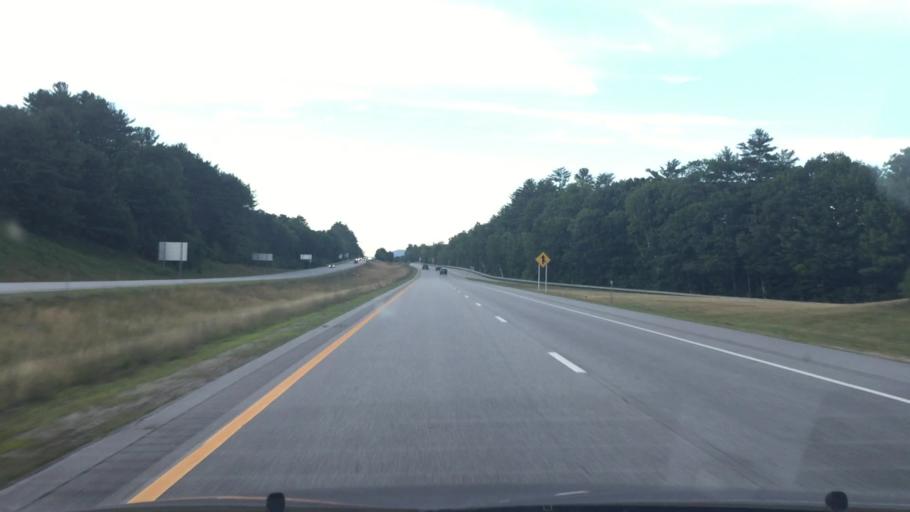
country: US
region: New Hampshire
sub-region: Grafton County
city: Plymouth
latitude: 43.7743
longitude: -71.6815
